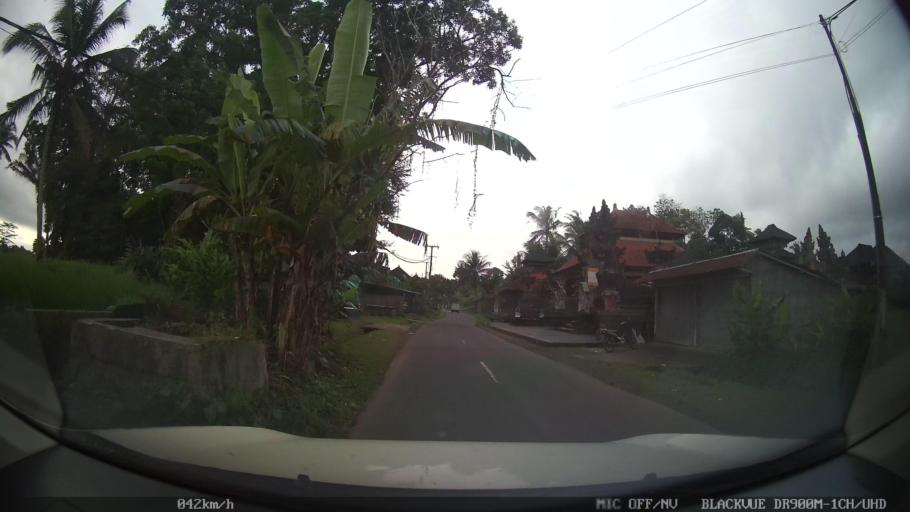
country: ID
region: Bali
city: Bunutan
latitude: -8.4790
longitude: 115.2585
